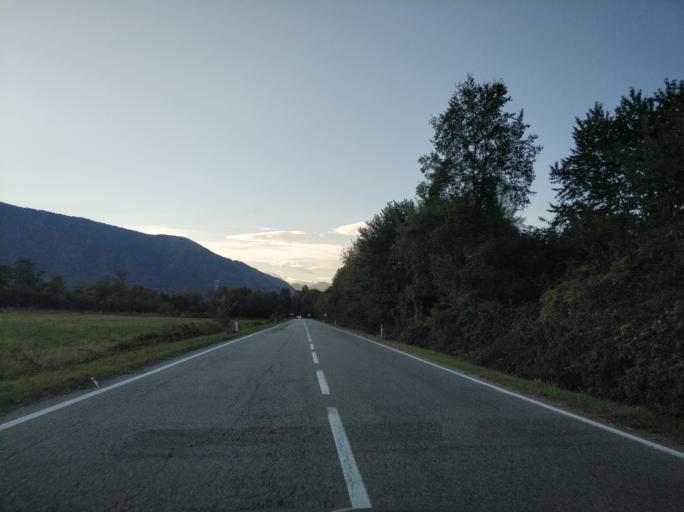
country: IT
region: Piedmont
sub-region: Provincia di Torino
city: Villanova Canavese
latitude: 45.2386
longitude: 7.5398
